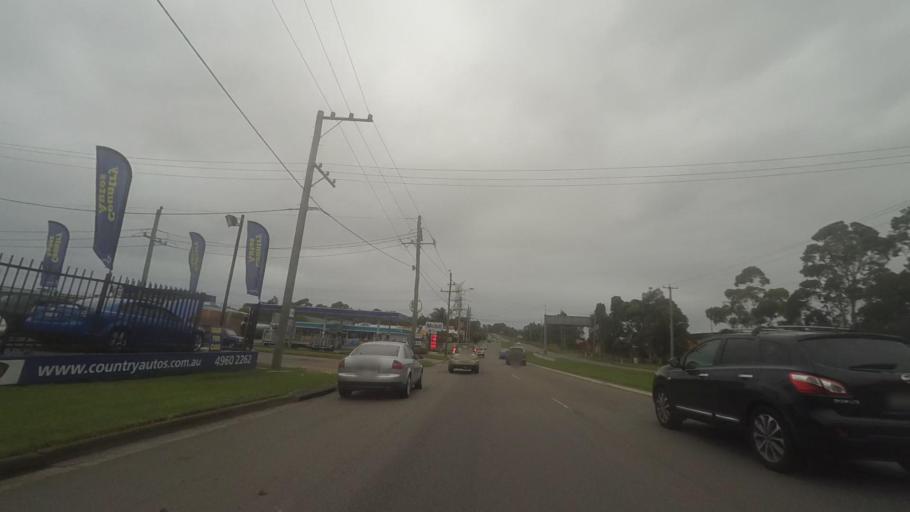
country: AU
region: New South Wales
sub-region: Newcastle
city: Mayfield West
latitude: -32.8728
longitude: 151.7115
